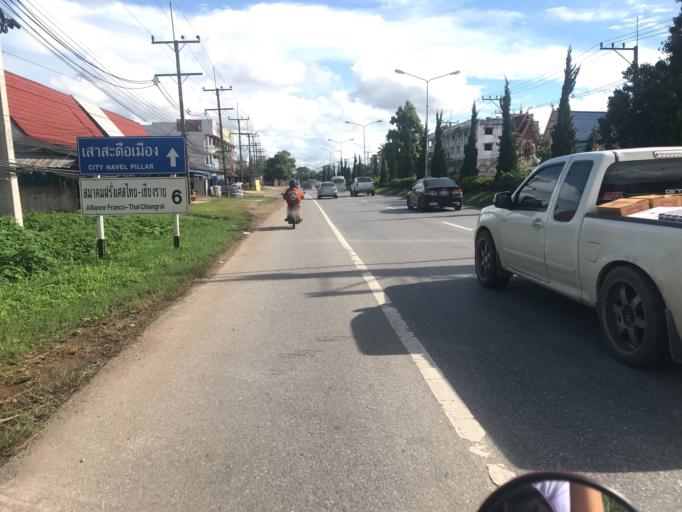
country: TH
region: Chiang Rai
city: Chiang Rai
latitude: 19.9557
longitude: 99.8513
